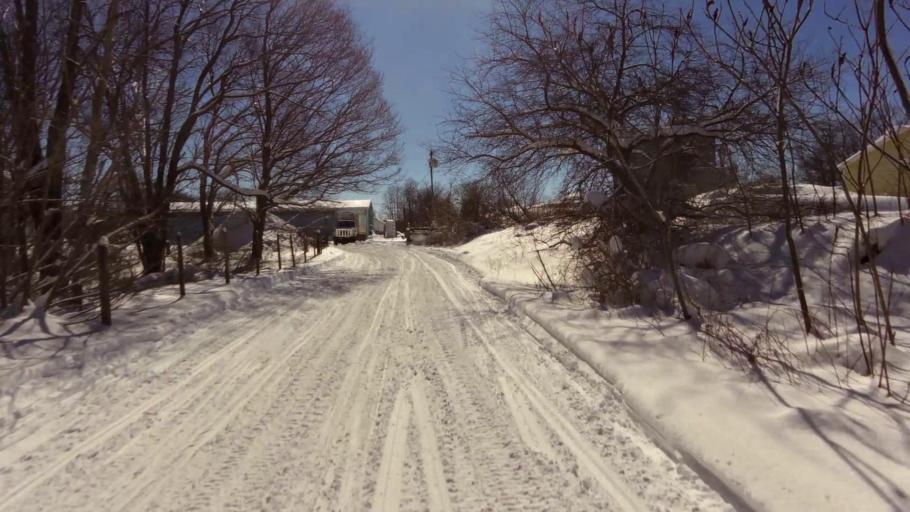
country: US
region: New York
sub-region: Chautauqua County
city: Mayville
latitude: 42.1655
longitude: -79.5841
